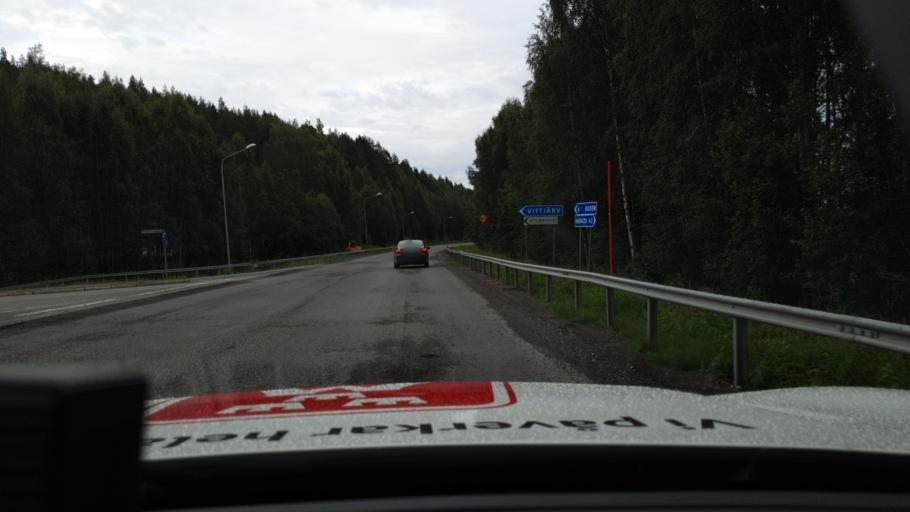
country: SE
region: Norrbotten
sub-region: Bodens Kommun
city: Boden
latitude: 65.8457
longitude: 21.5978
